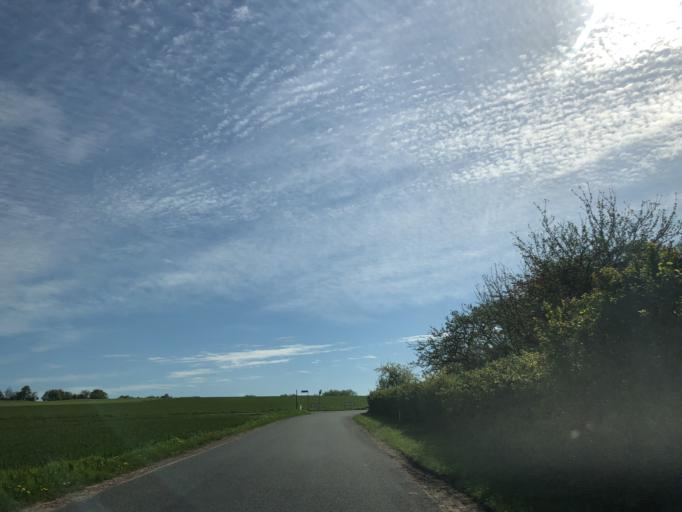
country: DK
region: Zealand
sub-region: Slagelse Kommune
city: Forlev
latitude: 55.3802
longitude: 11.2964
